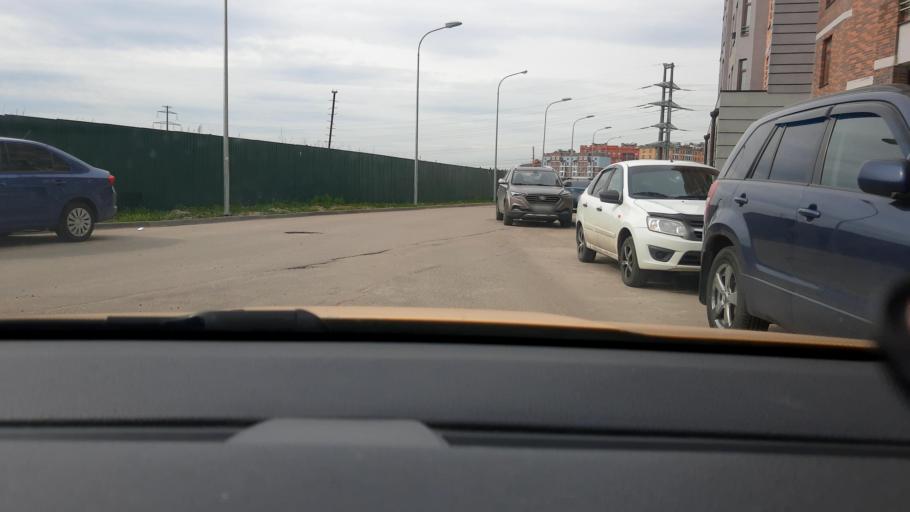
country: RU
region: Moskovskaya
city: Opalikha
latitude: 55.8805
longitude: 37.2691
